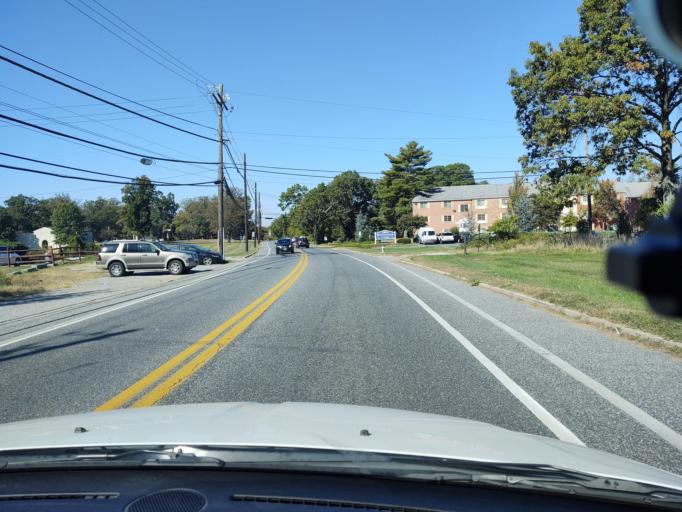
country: US
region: Maryland
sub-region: Prince George's County
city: Silver Hill
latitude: 38.8544
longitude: -76.9385
